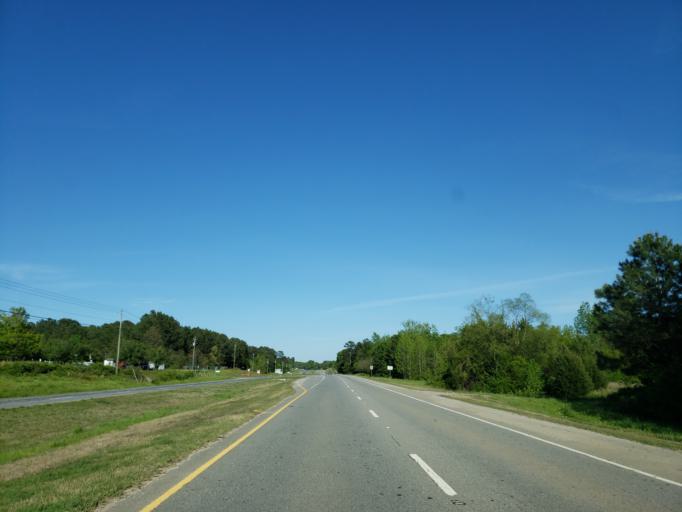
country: US
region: Georgia
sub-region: Polk County
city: Cedartown
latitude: 34.0037
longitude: -85.1643
